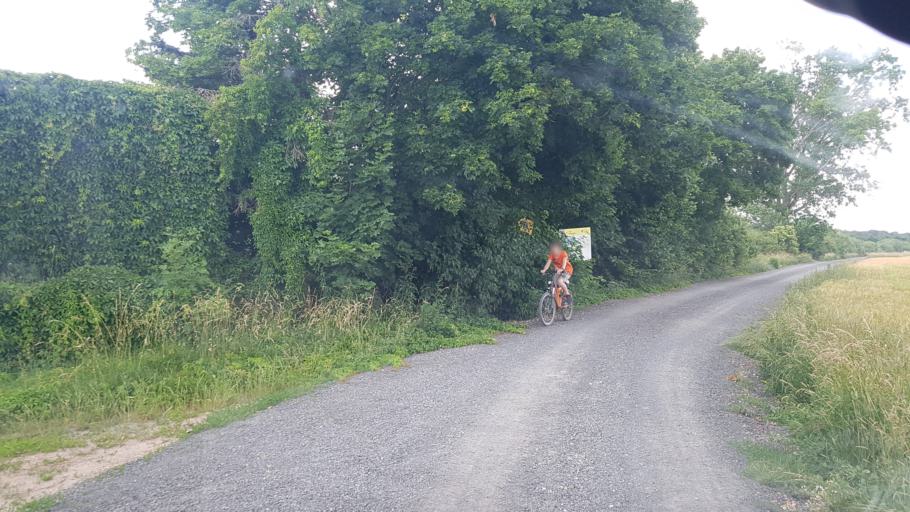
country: DE
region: Brandenburg
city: Plessa
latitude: 51.5365
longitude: 13.6335
